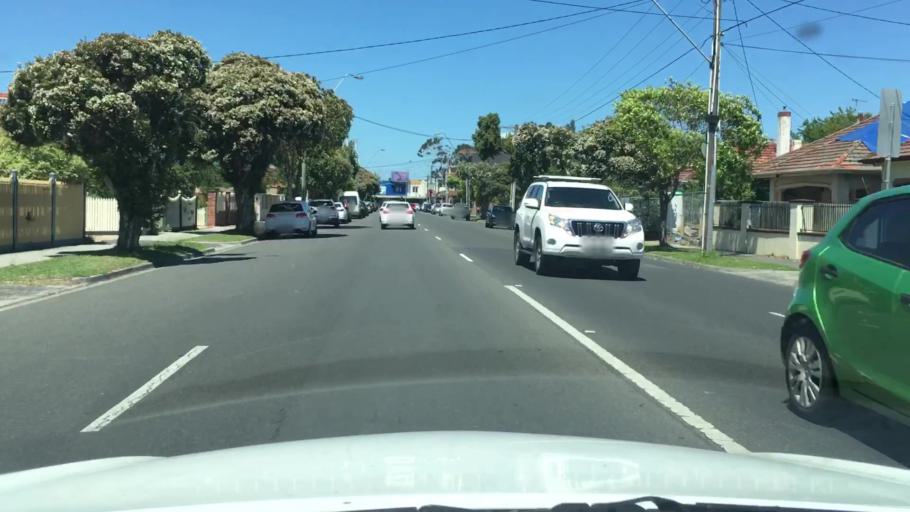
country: AU
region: Victoria
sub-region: Glen Eira
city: Glen Huntly
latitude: -37.8876
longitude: 145.0460
